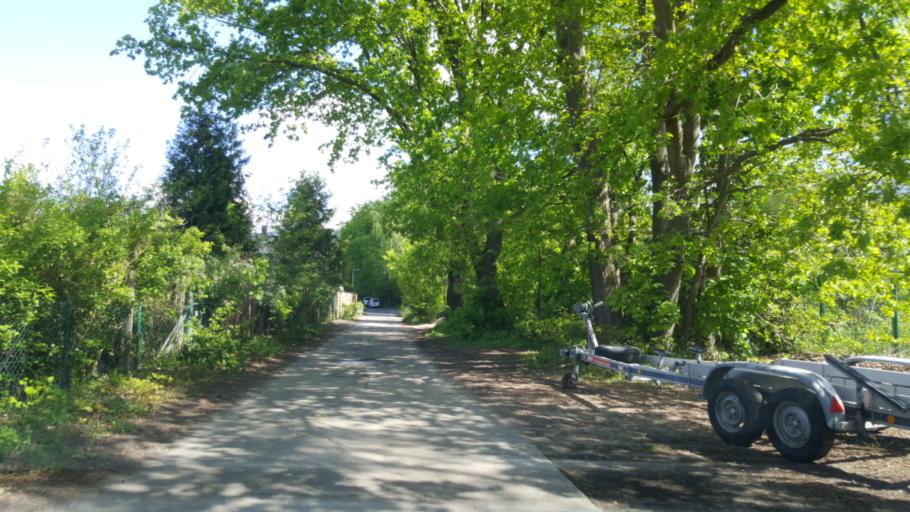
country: DE
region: Berlin
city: Berlin Koepenick
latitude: 52.4462
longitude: 13.5998
